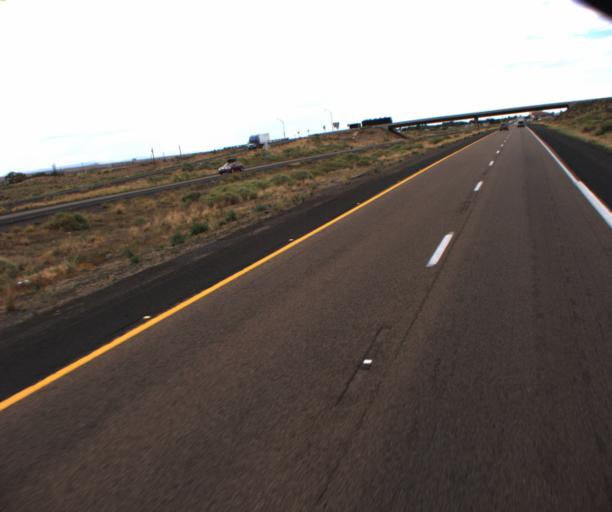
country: US
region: Arizona
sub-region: Navajo County
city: Joseph City
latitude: 34.9516
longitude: -110.3080
